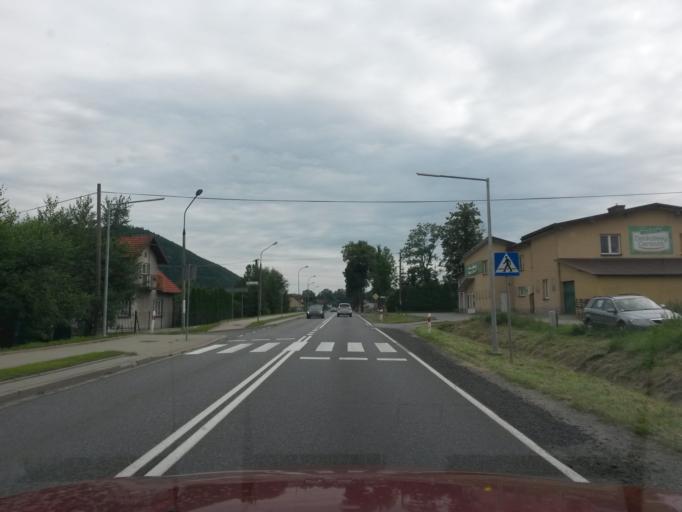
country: PL
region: Lesser Poland Voivodeship
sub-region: Powiat nowosadecki
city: Nawojowa
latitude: 49.5544
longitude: 20.7570
